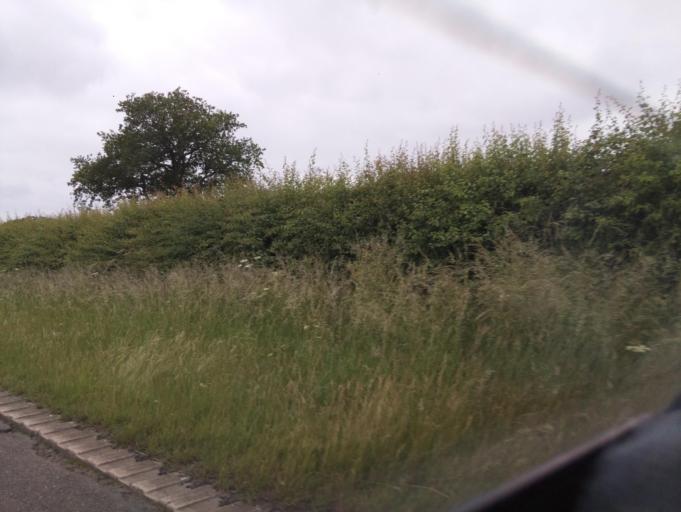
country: GB
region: England
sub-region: District of Rutland
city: Edith Weston
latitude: 52.6479
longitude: -0.6119
